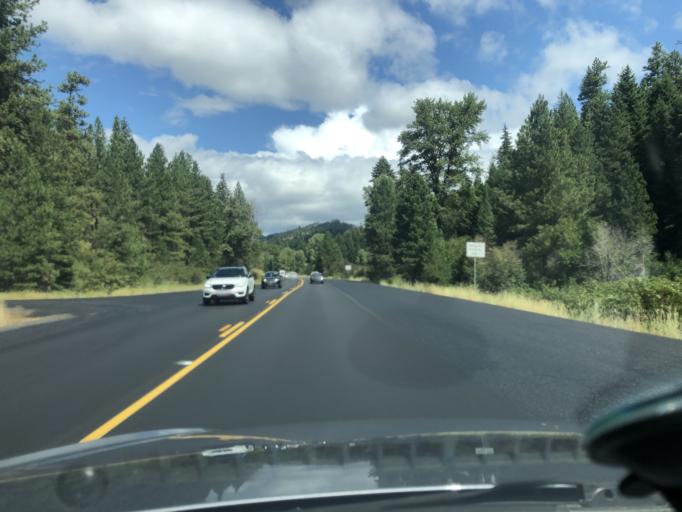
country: US
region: Washington
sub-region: Kittitas County
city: Cle Elum
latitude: 47.3093
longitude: -120.6939
